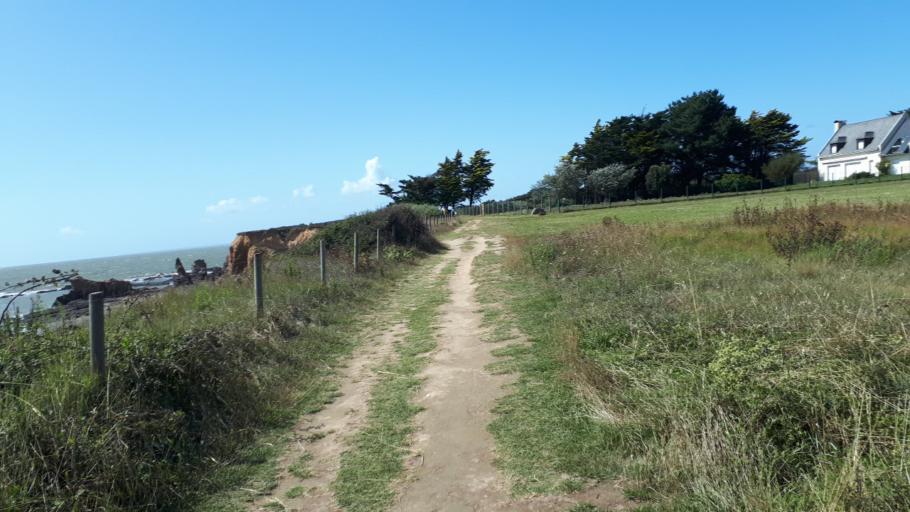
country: FR
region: Brittany
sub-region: Departement du Morbihan
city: Penestin
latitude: 47.4451
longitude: -2.4861
